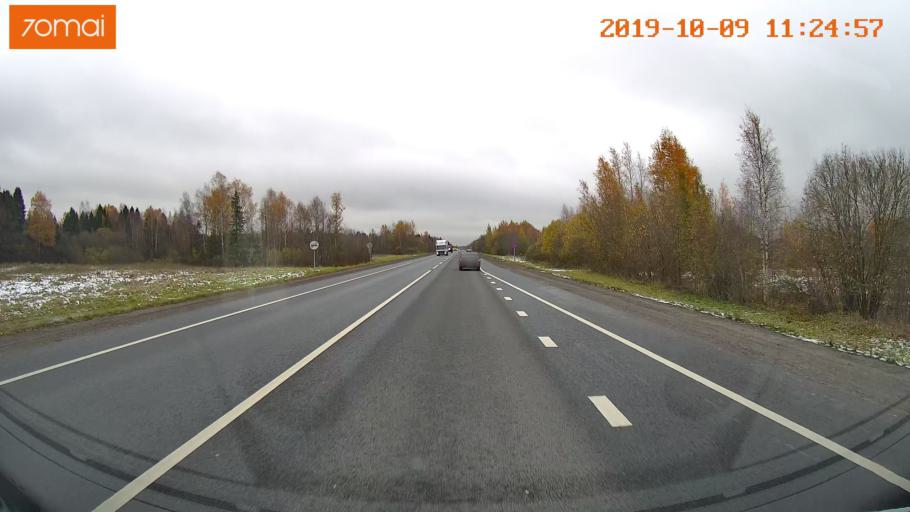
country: RU
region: Vologda
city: Vologda
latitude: 59.1064
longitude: 39.9856
